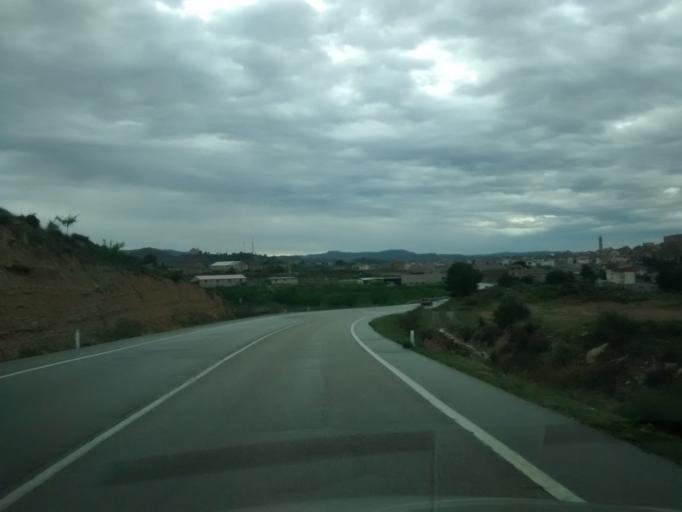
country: ES
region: Aragon
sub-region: Provincia de Zaragoza
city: Maella
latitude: 41.1149
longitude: 0.1487
